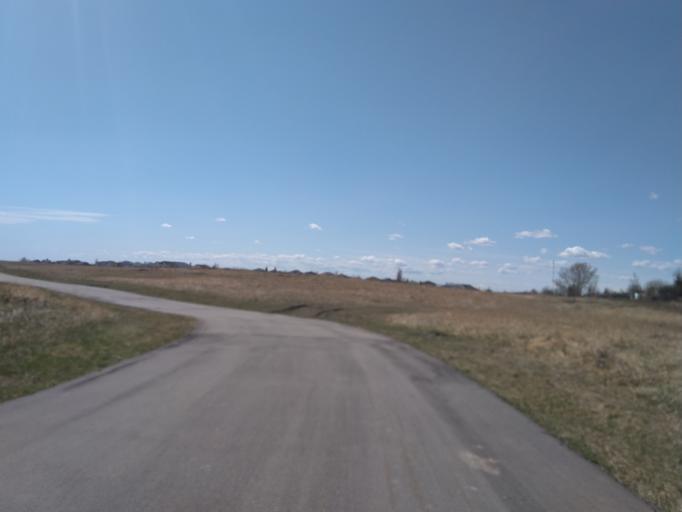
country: CA
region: Alberta
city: Chestermere
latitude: 51.0546
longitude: -113.9230
